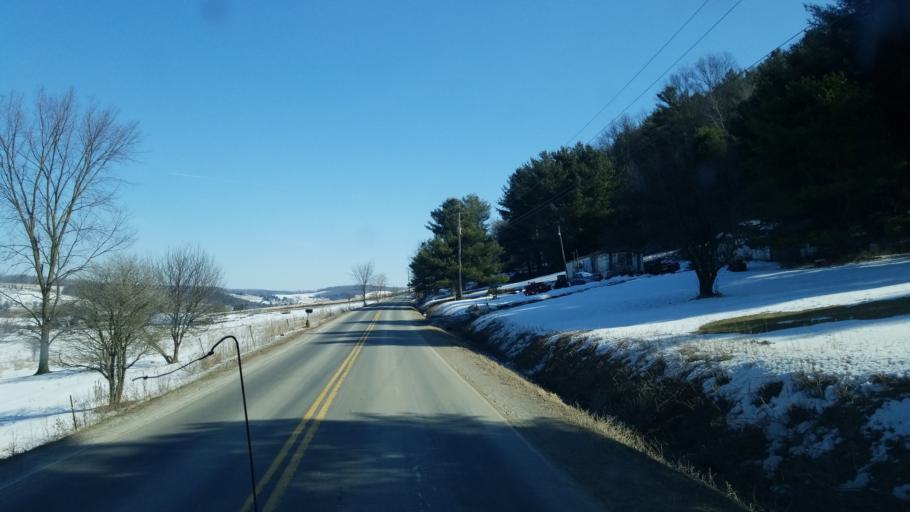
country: US
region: Pennsylvania
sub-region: Tioga County
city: Elkland
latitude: 42.0672
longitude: -77.4341
